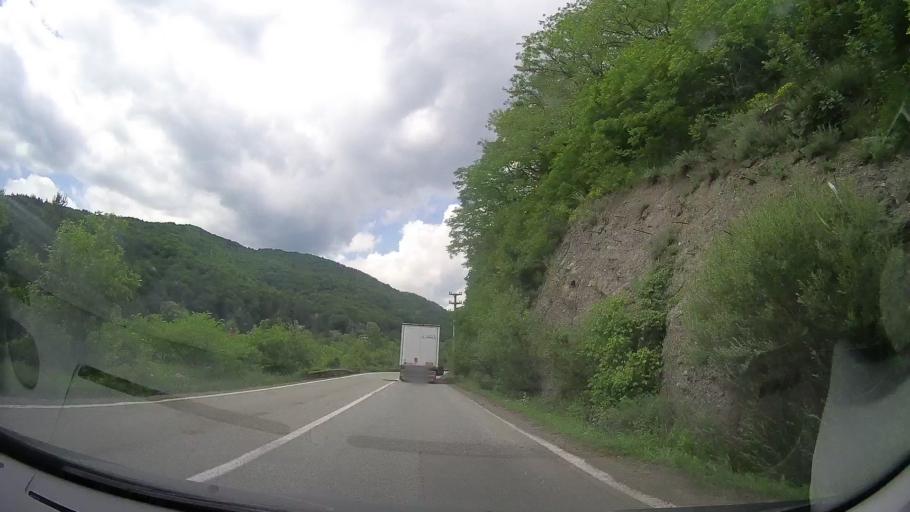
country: RO
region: Valcea
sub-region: Oras Calimanesti
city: Jiblea Veche
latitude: 45.2489
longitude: 24.3418
